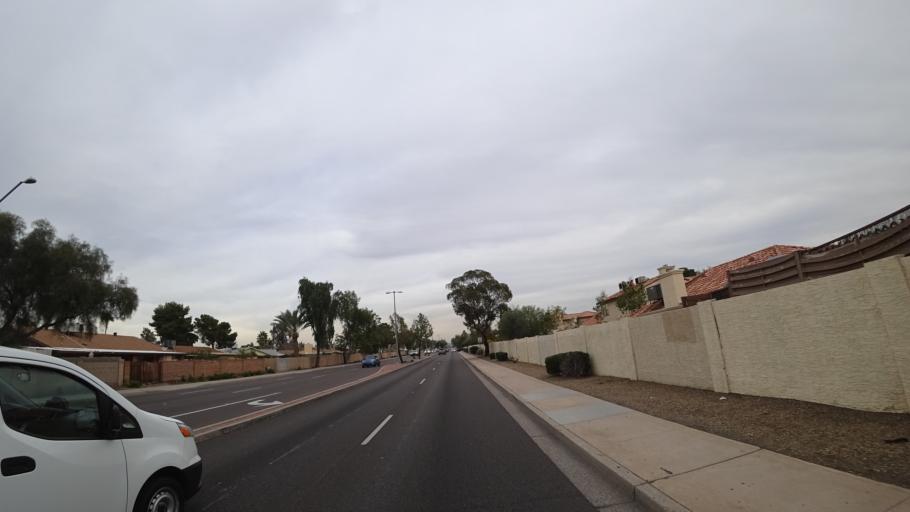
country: US
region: Arizona
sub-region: Maricopa County
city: Glendale
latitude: 33.5819
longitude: -112.1772
